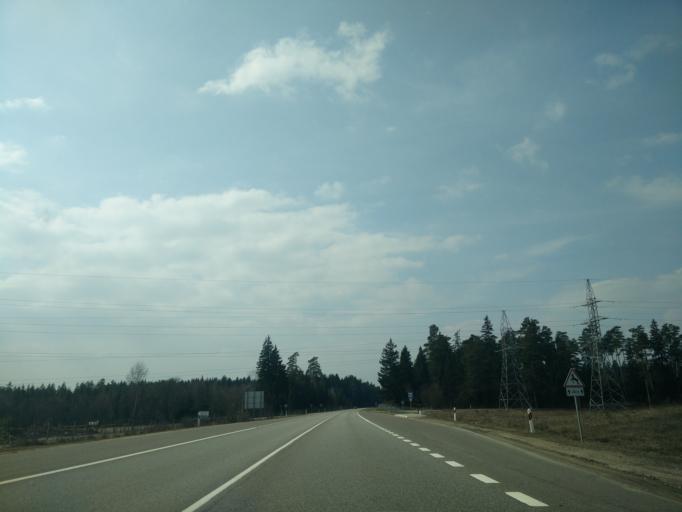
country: LT
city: Lentvaris
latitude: 54.6199
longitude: 25.0908
